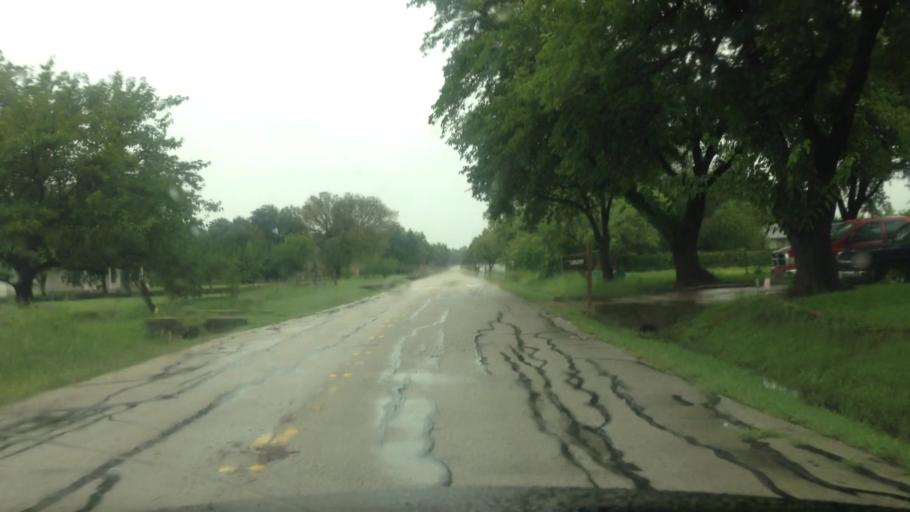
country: US
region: Texas
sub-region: Tarrant County
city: Watauga
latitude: 32.8681
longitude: -97.2254
